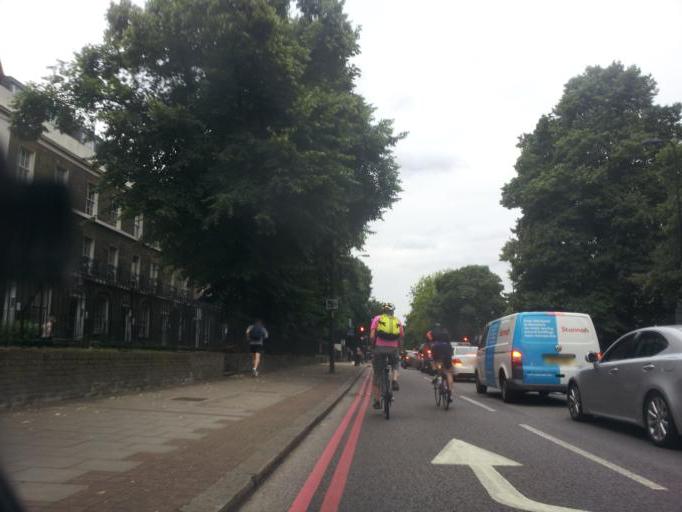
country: GB
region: England
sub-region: Greater London
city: Kennington
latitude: 51.4774
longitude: -0.1122
